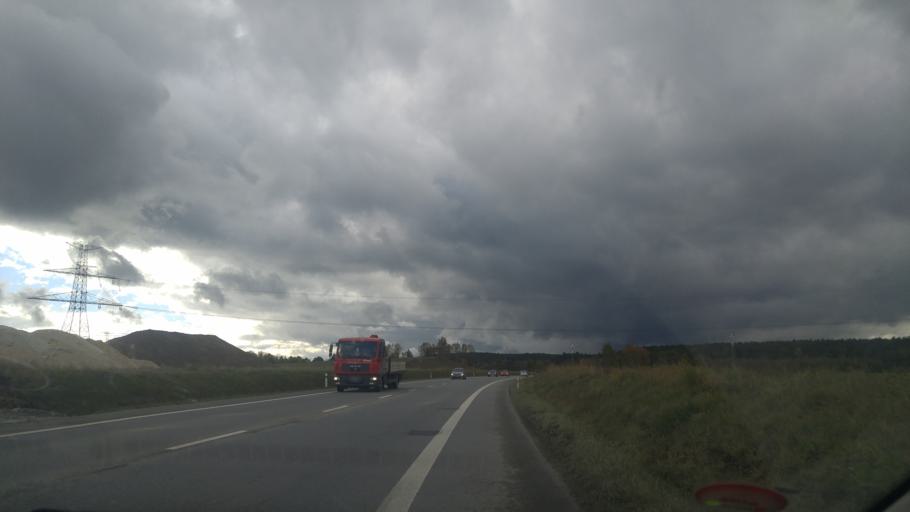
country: CZ
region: Jihocesky
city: Sevetin
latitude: 49.1149
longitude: 14.5842
